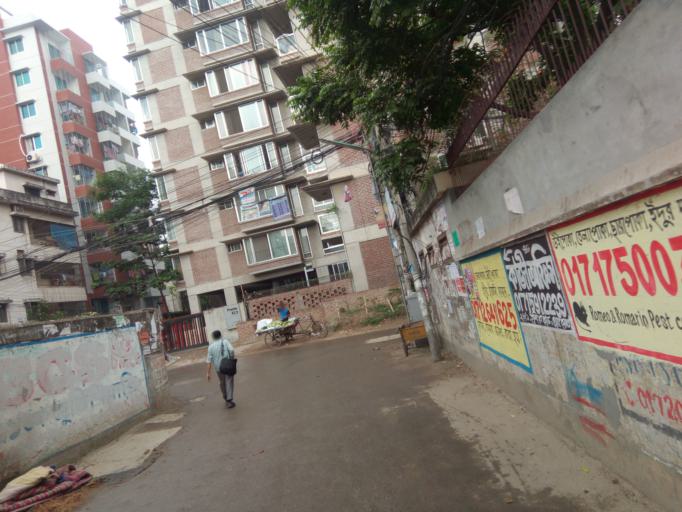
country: BD
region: Dhaka
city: Azimpur
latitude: 23.7560
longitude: 90.3842
